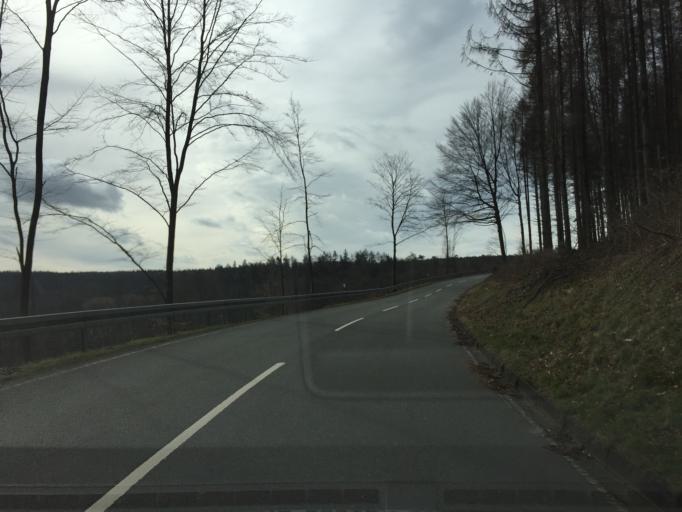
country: DE
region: North Rhine-Westphalia
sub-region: Regierungsbezirk Detmold
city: Detmold
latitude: 51.9105
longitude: 8.8458
